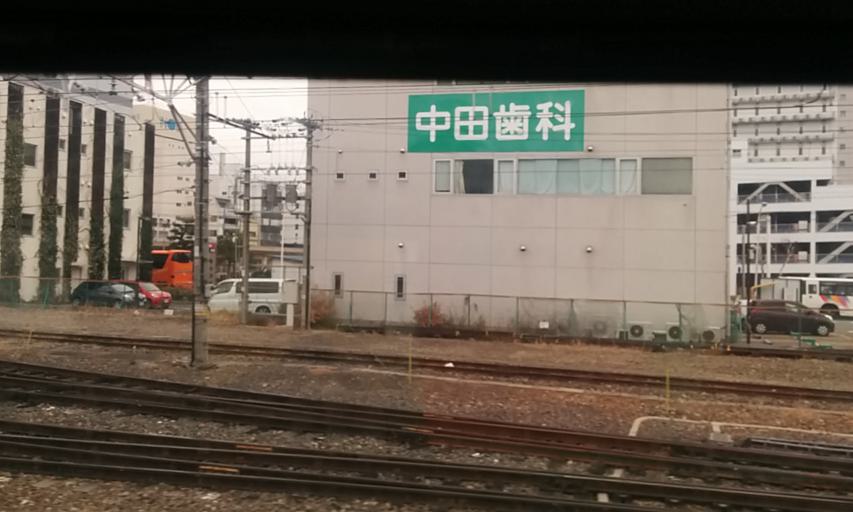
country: JP
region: Nagano
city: Matsumoto
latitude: 36.2278
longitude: 137.9661
